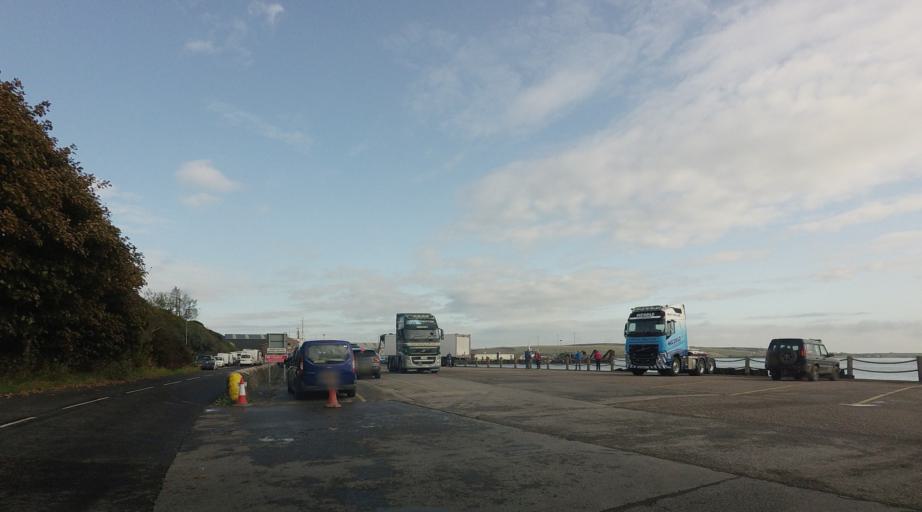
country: GB
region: Scotland
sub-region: Orkney Islands
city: Orkney
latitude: 58.8306
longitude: -2.9628
